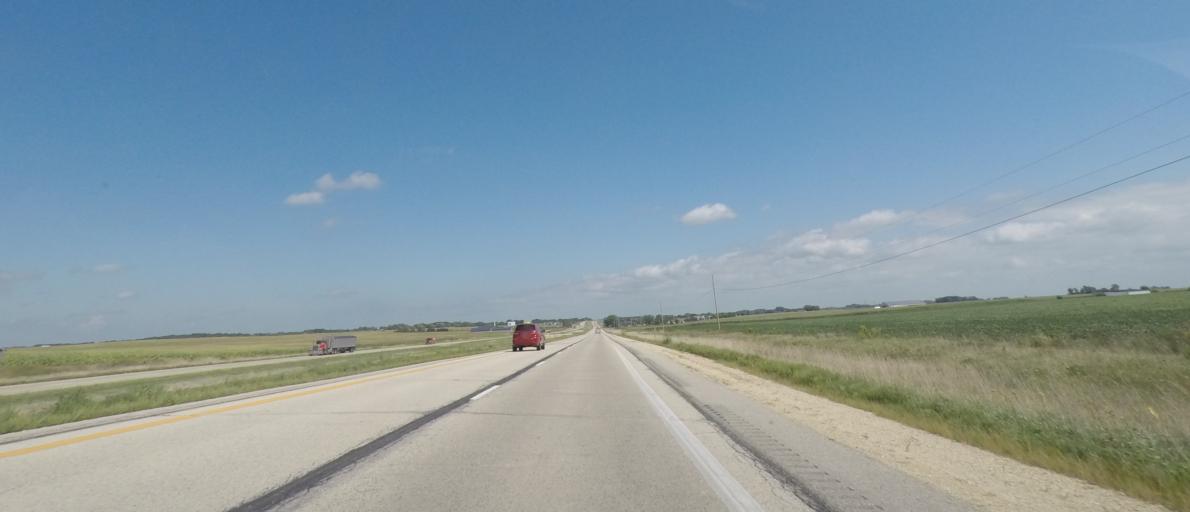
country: US
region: Iowa
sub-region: Jones County
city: Anamosa
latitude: 42.0707
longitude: -91.3596
